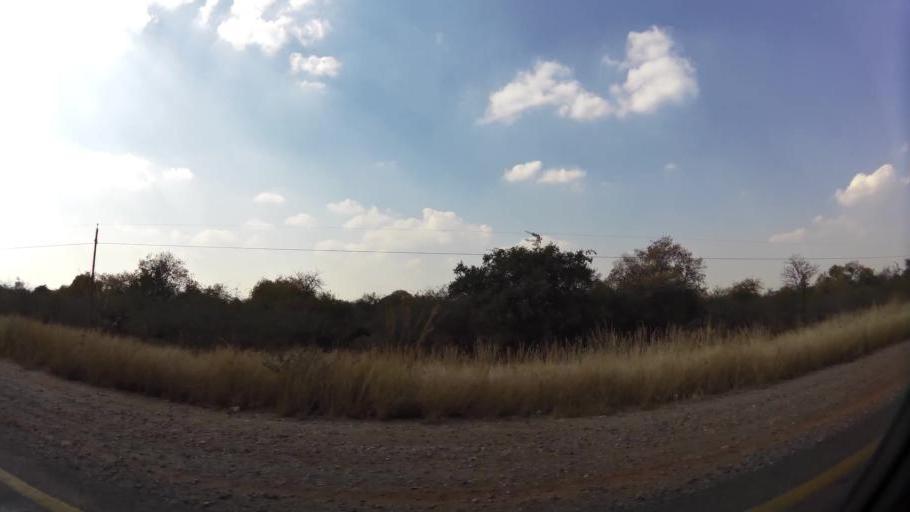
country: ZA
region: North-West
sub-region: Bojanala Platinum District Municipality
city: Rustenburg
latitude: -25.5356
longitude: 27.1198
